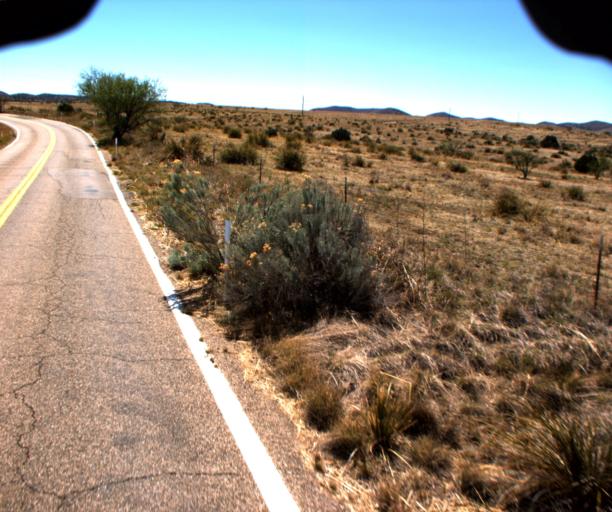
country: US
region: Arizona
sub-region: Cochise County
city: Huachuca City
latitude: 31.5872
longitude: -110.5623
